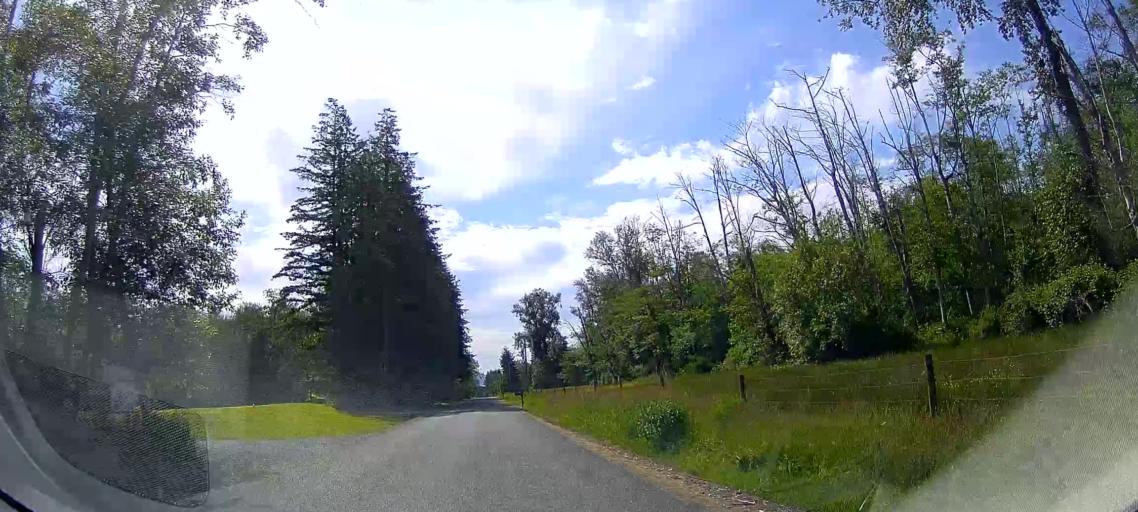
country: US
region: Washington
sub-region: Skagit County
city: Burlington
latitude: 48.5447
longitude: -122.3640
